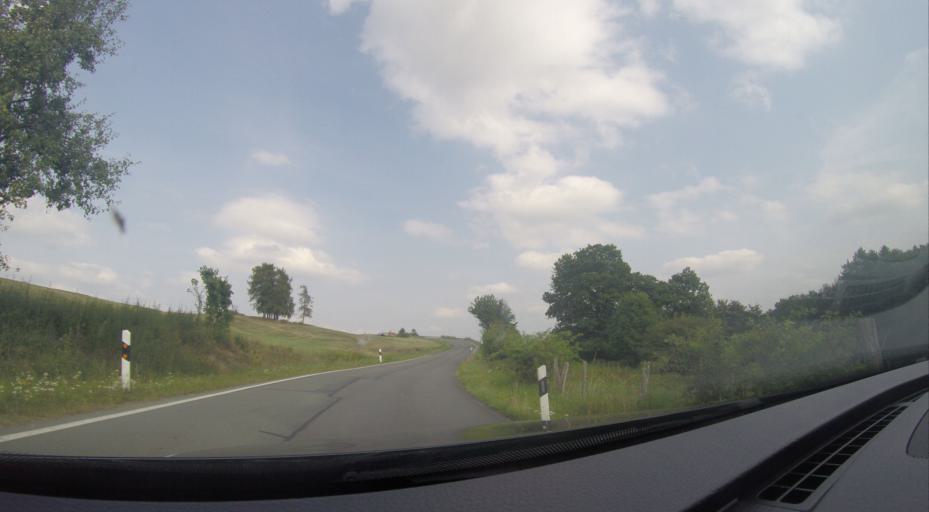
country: DE
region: North Rhine-Westphalia
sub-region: Regierungsbezirk Arnsberg
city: Medebach
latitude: 51.1777
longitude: 8.6664
